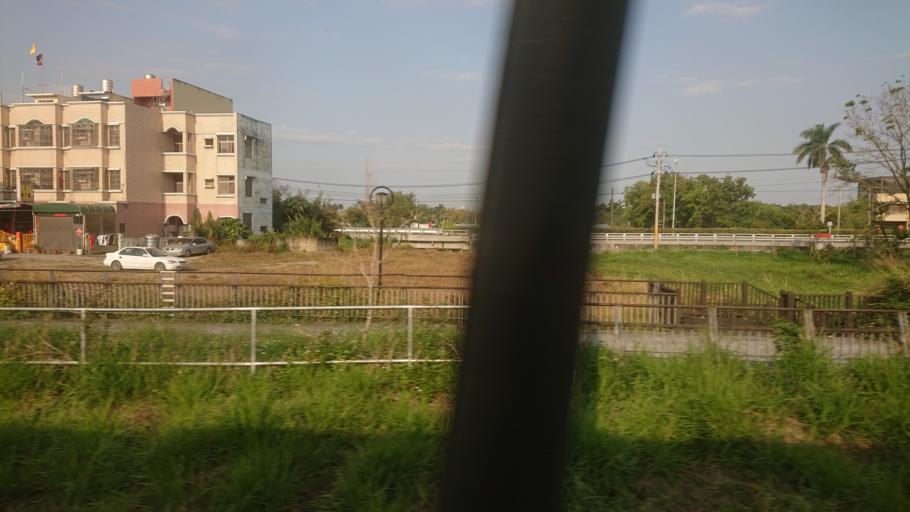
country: TW
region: Taiwan
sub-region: Chiayi
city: Jiayi Shi
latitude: 23.6073
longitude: 120.4603
